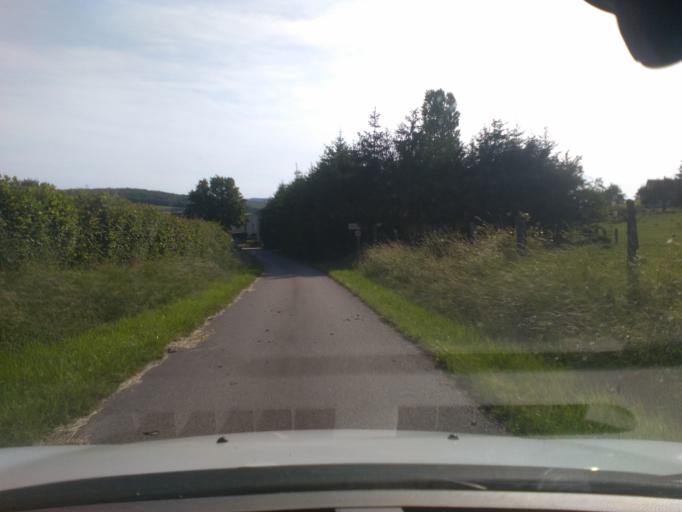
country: FR
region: Lorraine
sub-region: Departement des Vosges
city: Mirecourt
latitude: 48.2581
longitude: 6.1965
